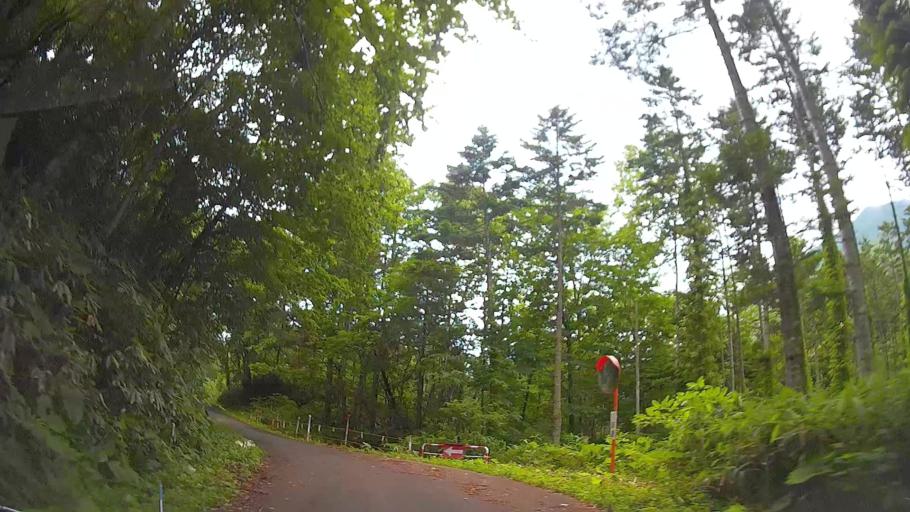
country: JP
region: Hokkaido
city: Nanae
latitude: 42.0506
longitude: 140.4931
